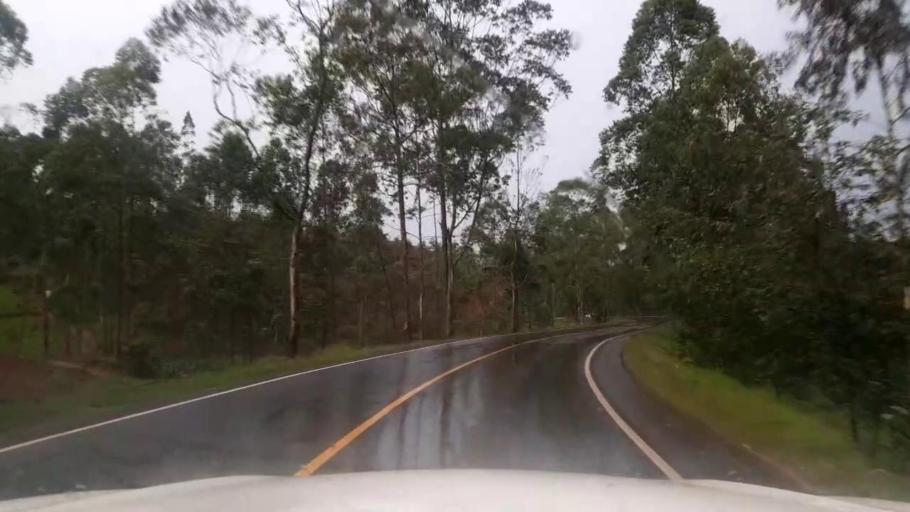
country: RW
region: Northern Province
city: Musanze
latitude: -1.5840
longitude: 29.7348
